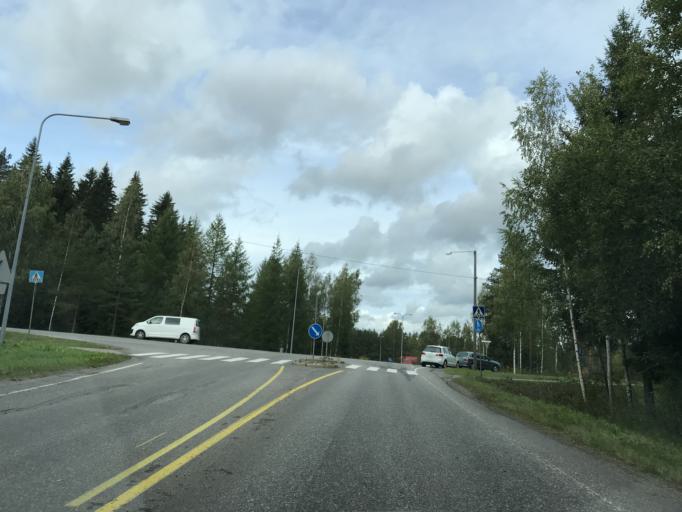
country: FI
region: Paijanne Tavastia
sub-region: Lahti
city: Lahti
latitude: 61.0013
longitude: 25.7776
